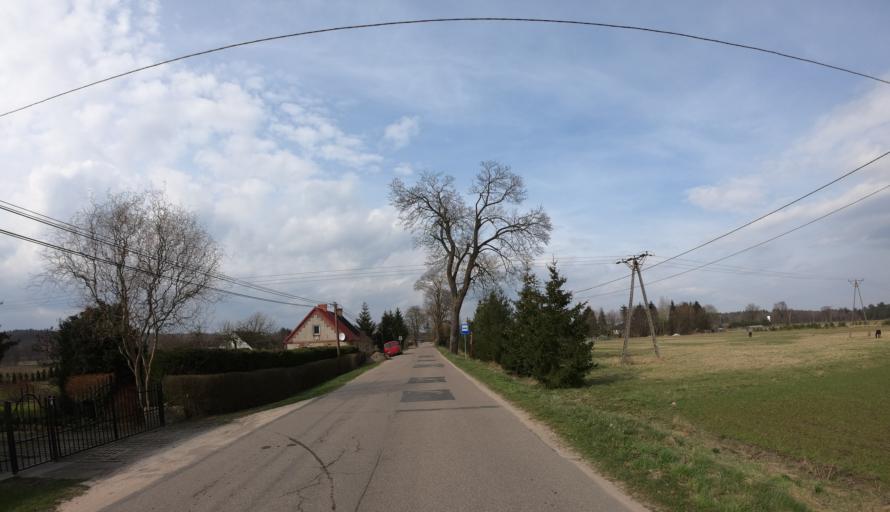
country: PL
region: West Pomeranian Voivodeship
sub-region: Powiat swidwinski
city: Swidwin
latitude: 53.8099
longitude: 15.7946
